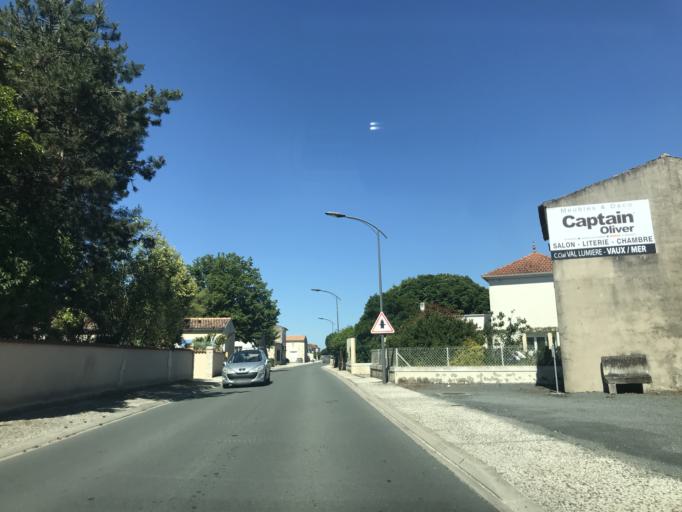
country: FR
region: Poitou-Charentes
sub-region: Departement de la Charente-Maritime
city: Gemozac
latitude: 45.5654
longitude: -0.7238
